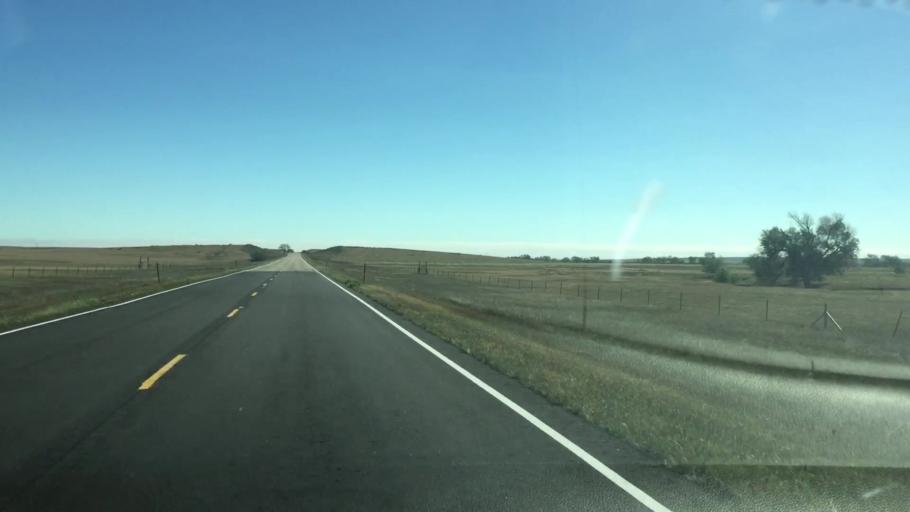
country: US
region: Colorado
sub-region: Lincoln County
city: Limon
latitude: 39.2943
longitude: -103.9061
